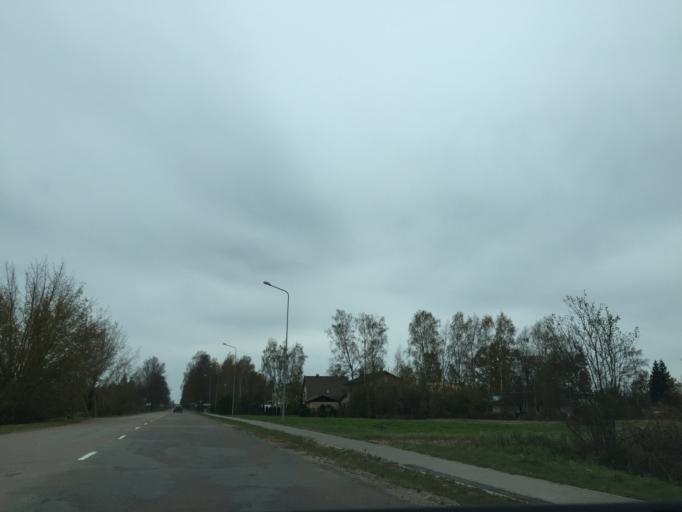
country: LV
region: Marupe
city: Marupe
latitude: 56.8797
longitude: 24.0677
